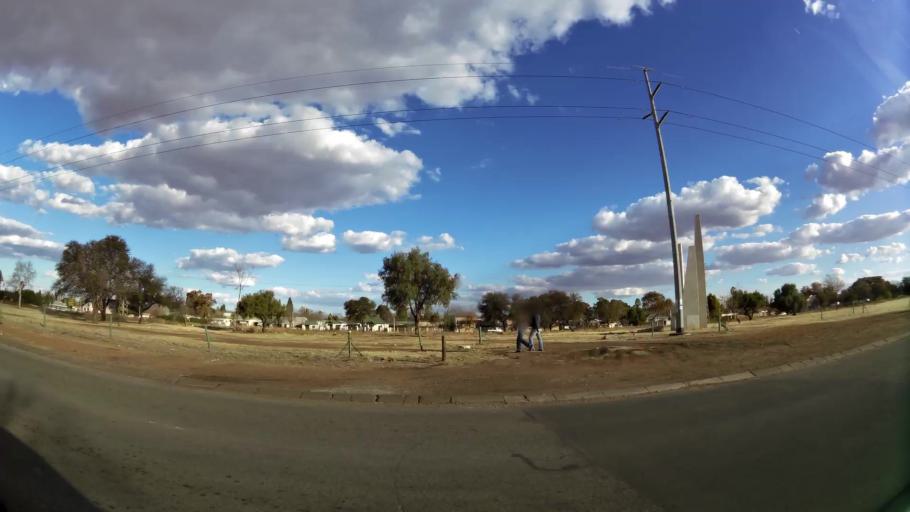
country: ZA
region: North-West
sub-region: Dr Kenneth Kaunda District Municipality
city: Potchefstroom
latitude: -26.7004
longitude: 27.0961
